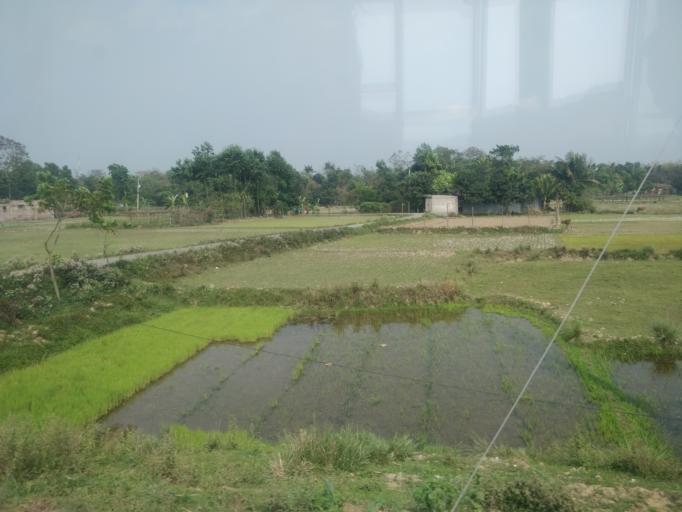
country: BD
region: Sylhet
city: Habiganj
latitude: 24.3241
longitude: 91.4336
